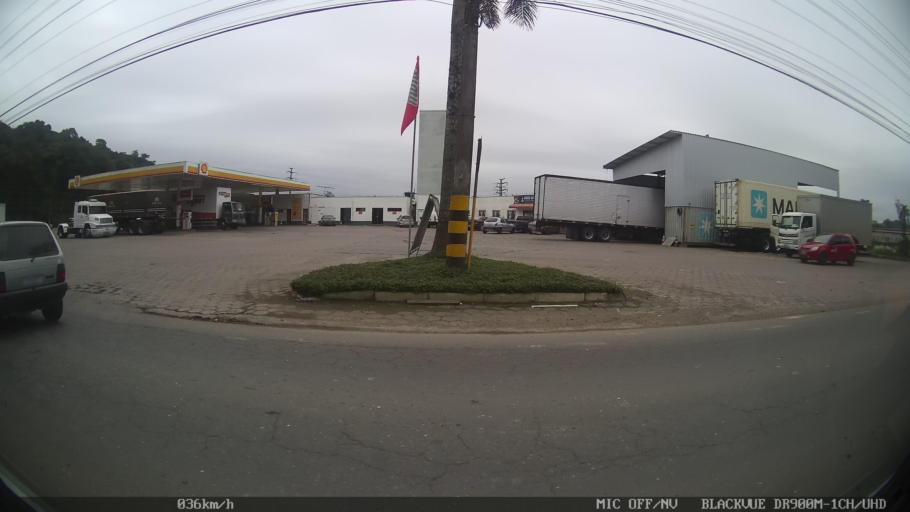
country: BR
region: Santa Catarina
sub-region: Joinville
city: Joinville
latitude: -26.2471
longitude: -48.8799
